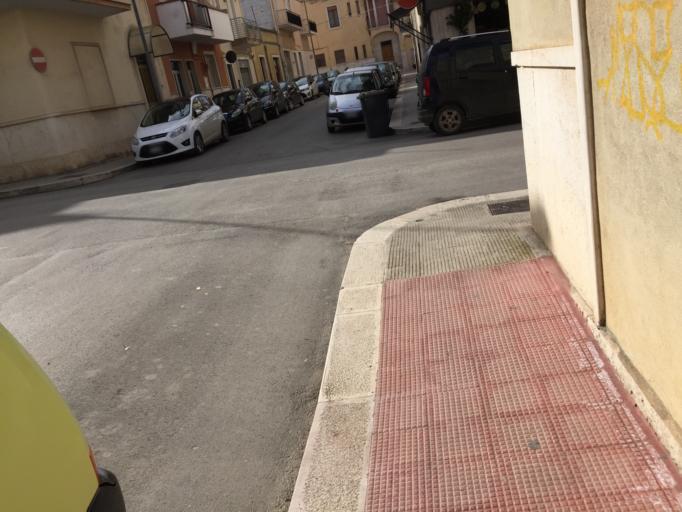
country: IT
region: Apulia
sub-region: Provincia di Barletta - Andria - Trani
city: Andria
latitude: 41.2229
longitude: 16.3050
